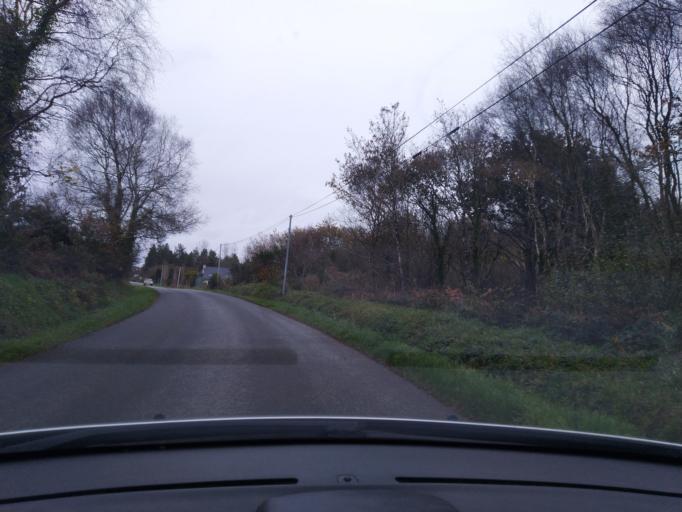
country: FR
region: Brittany
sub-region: Departement du Finistere
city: Guerlesquin
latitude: 48.5621
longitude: -3.5457
